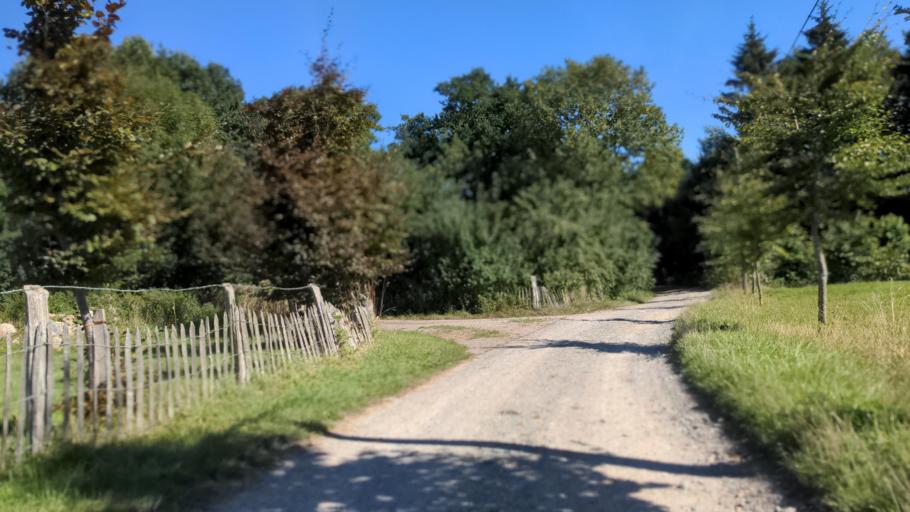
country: DE
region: Mecklenburg-Vorpommern
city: Klutz
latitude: 53.9809
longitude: 11.1368
